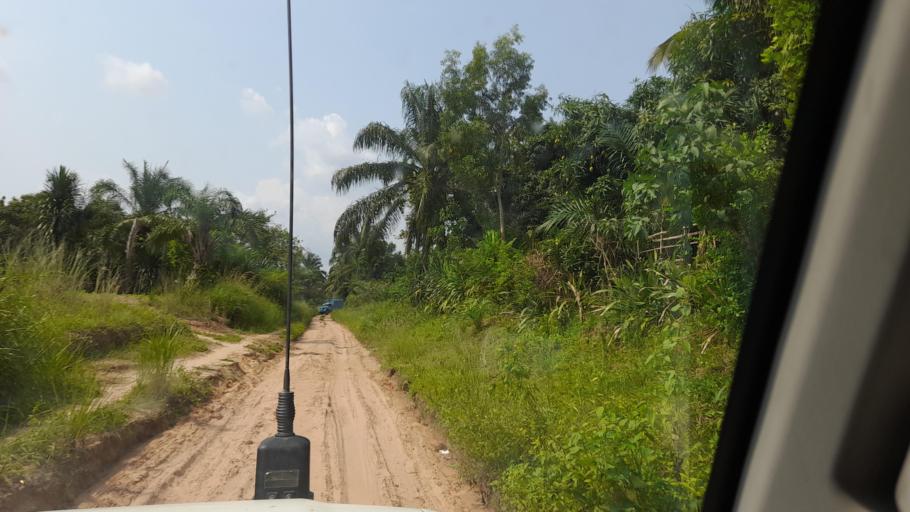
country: CD
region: Kasai-Occidental
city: Kananga
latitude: -5.9189
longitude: 22.4781
